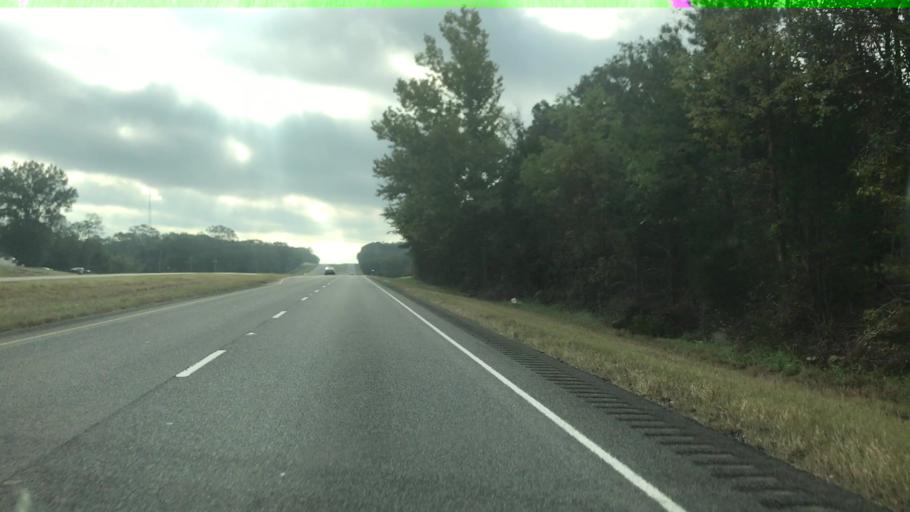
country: US
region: Alabama
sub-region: Morgan County
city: Danville
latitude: 34.4031
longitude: -87.1368
